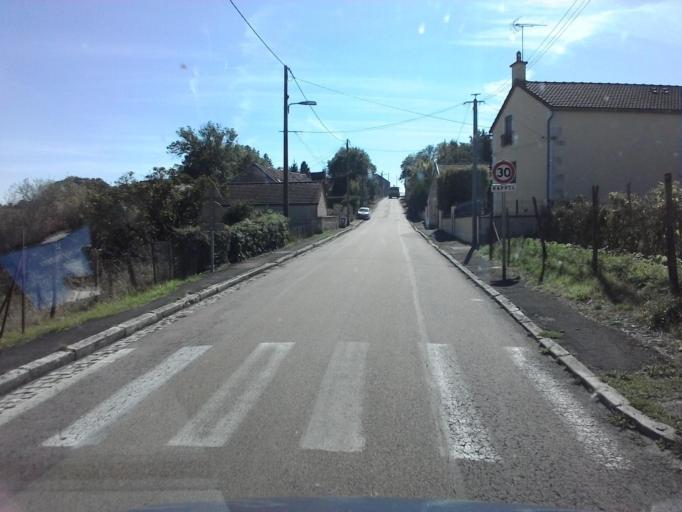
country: FR
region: Bourgogne
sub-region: Departement de l'Yonne
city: Tonnerre
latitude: 47.7922
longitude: 3.9466
